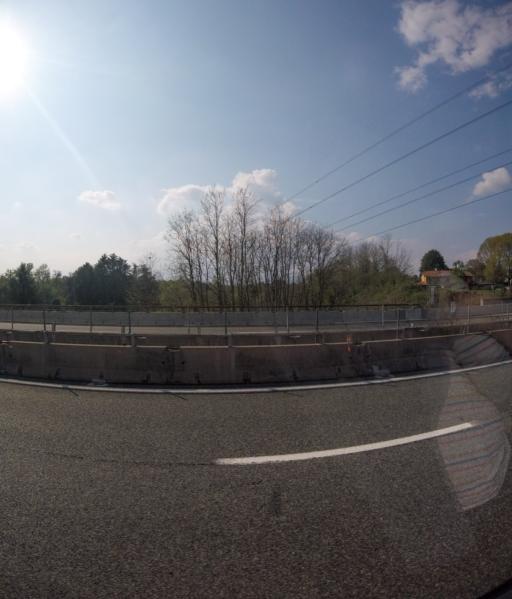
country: IT
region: Lombardy
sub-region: Provincia di Varese
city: Golasecca
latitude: 45.7047
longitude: 8.6475
